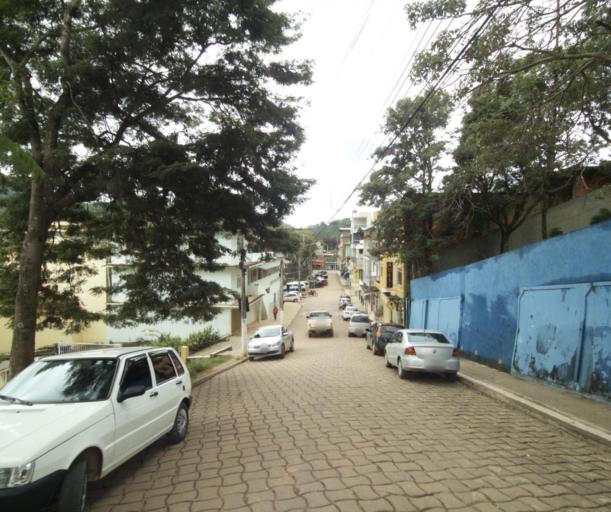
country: BR
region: Espirito Santo
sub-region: Irupi
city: Irupi
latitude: -20.3458
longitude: -41.6415
